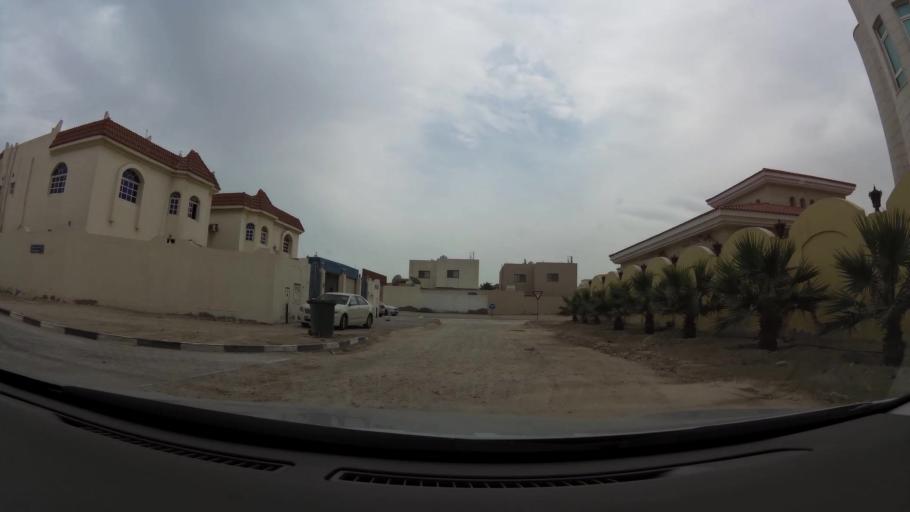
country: QA
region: Baladiyat ar Rayyan
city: Ar Rayyan
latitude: 25.3461
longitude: 51.4728
